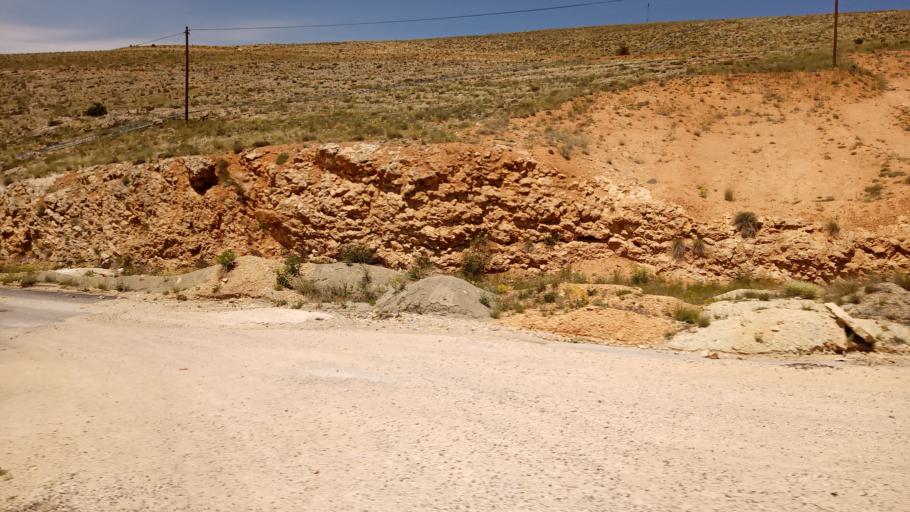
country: TR
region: Malatya
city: Darende
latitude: 38.5871
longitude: 37.4628
